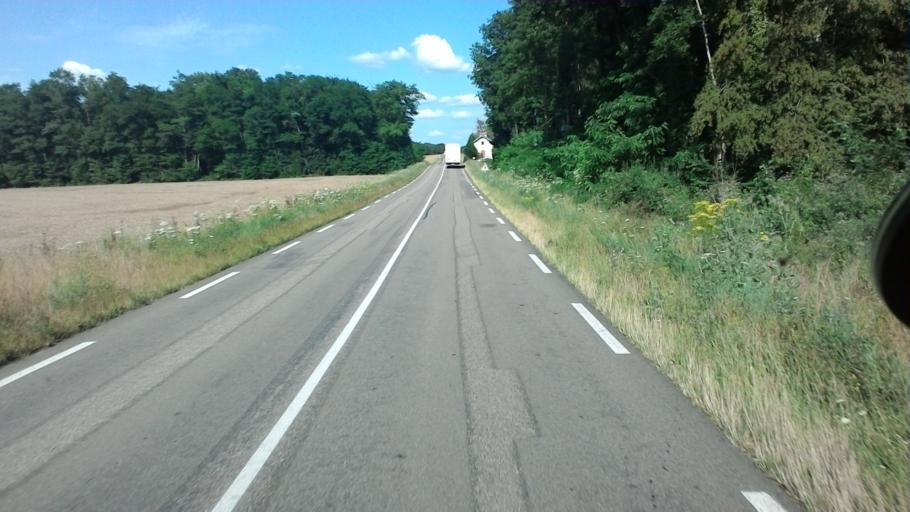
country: FR
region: Franche-Comte
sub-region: Departement de la Haute-Saone
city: Pesmes
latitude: 47.3044
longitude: 5.6421
